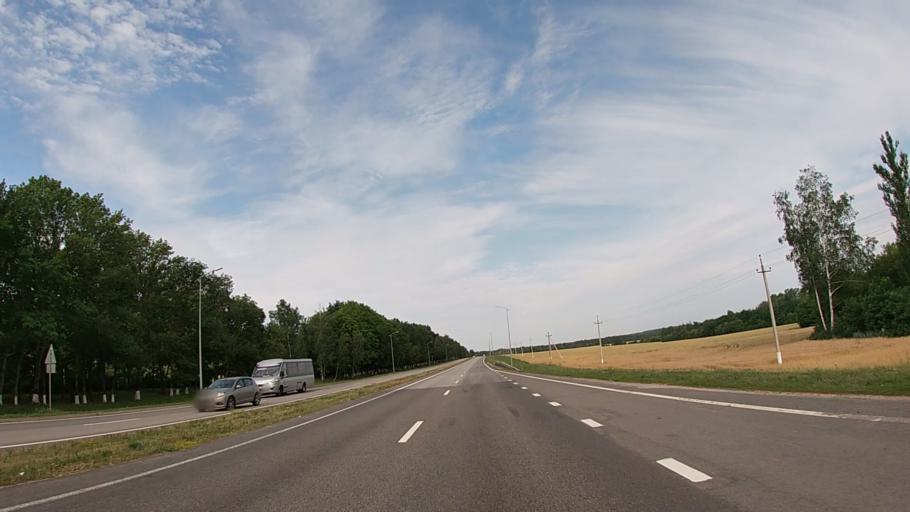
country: RU
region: Belgorod
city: Borisovka
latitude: 50.7517
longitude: 36.0128
